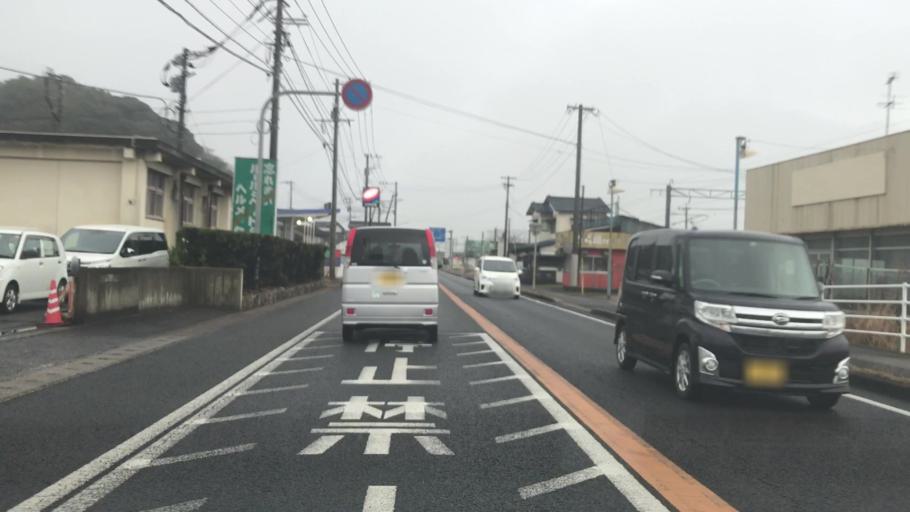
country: JP
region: Saga Prefecture
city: Takeocho-takeo
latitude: 33.2136
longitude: 130.0996
